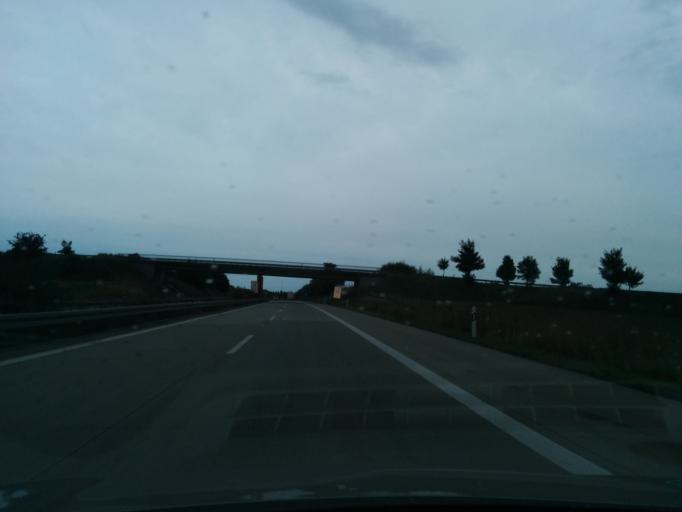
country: DE
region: Mecklenburg-Vorpommern
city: Strasburg
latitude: 53.5479
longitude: 13.6818
